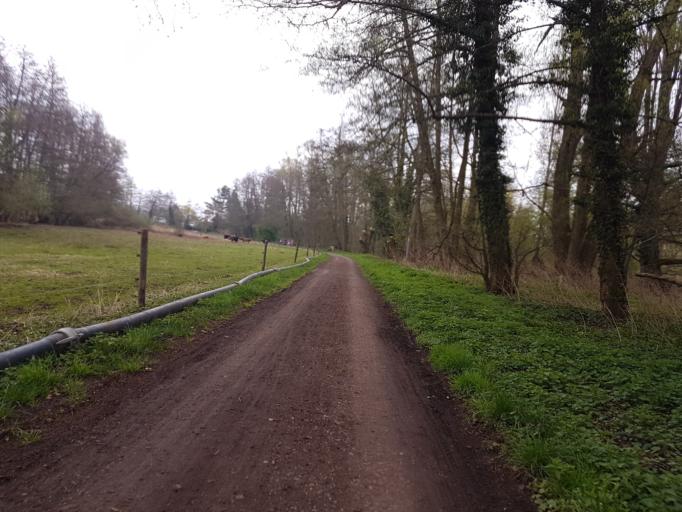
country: DE
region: Rheinland-Pfalz
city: Landau in der Pfalz
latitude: 49.2005
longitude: 8.0939
